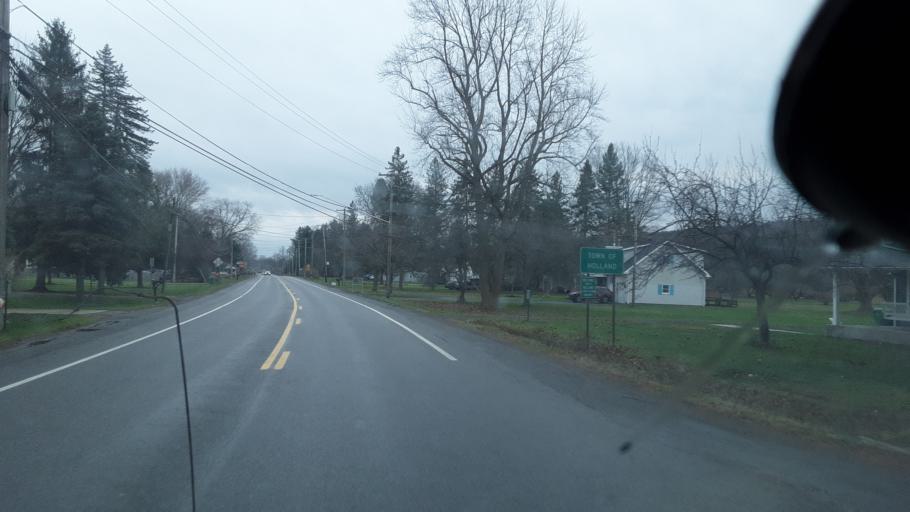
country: US
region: New York
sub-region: Erie County
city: Holland
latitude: 42.6930
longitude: -78.5713
